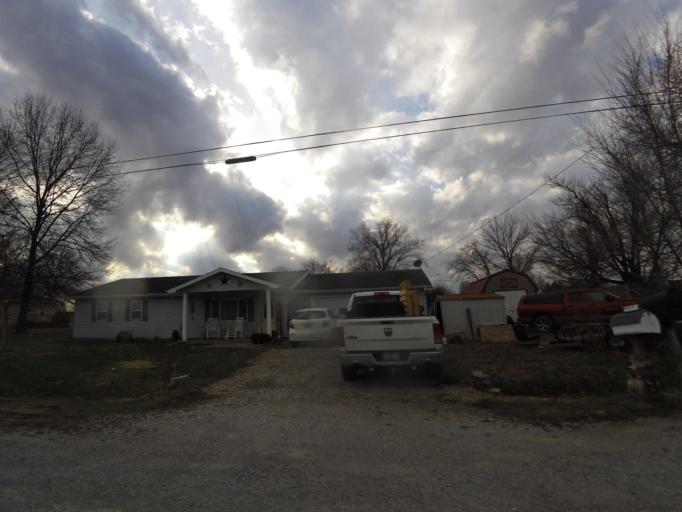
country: US
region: Illinois
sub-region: Fayette County
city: Ramsey
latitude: 39.1399
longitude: -89.1066
